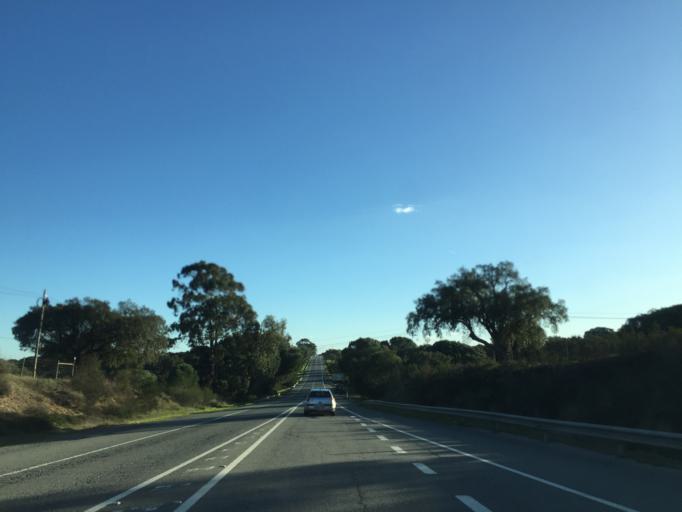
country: PT
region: Setubal
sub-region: Grandola
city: Grandola
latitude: 38.1126
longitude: -8.4182
